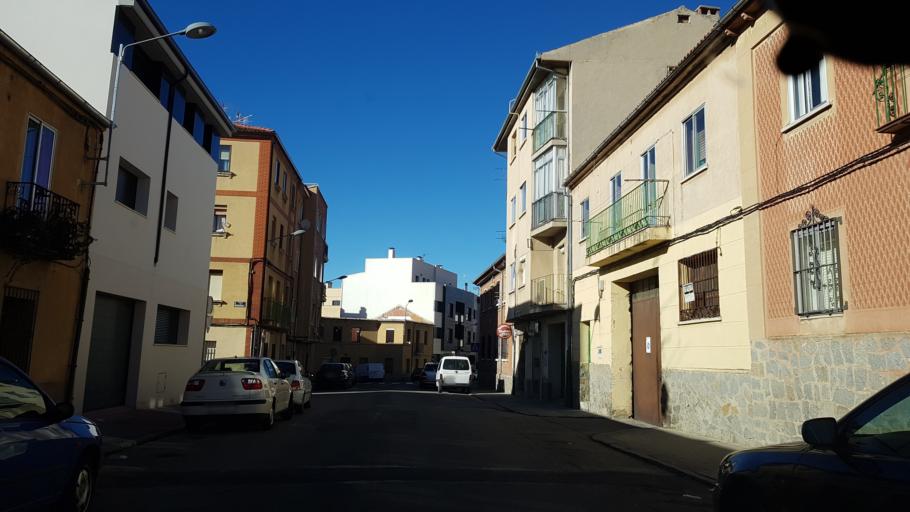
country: ES
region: Castille and Leon
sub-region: Provincia de Segovia
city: Segovia
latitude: 40.9446
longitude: -4.1073
